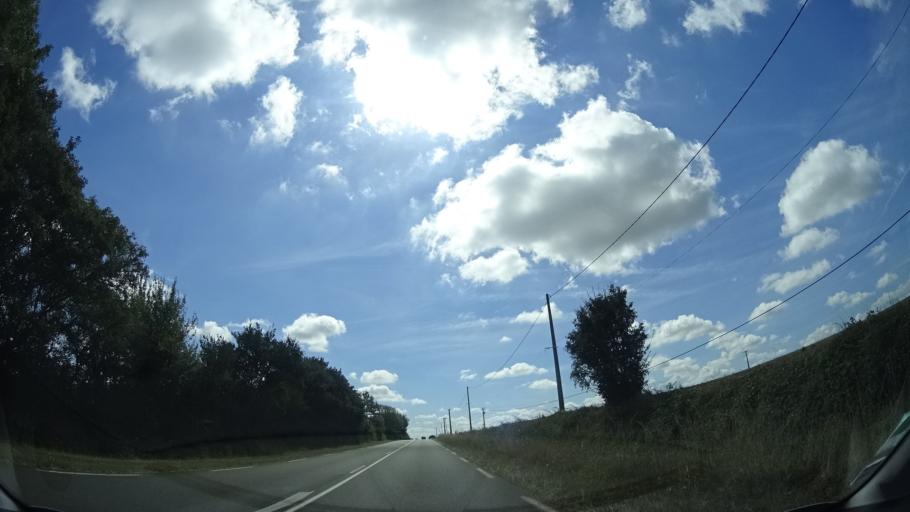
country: FR
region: Pays de la Loire
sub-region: Departement de la Mayenne
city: Meslay-du-Maine
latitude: 47.9164
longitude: -0.4690
